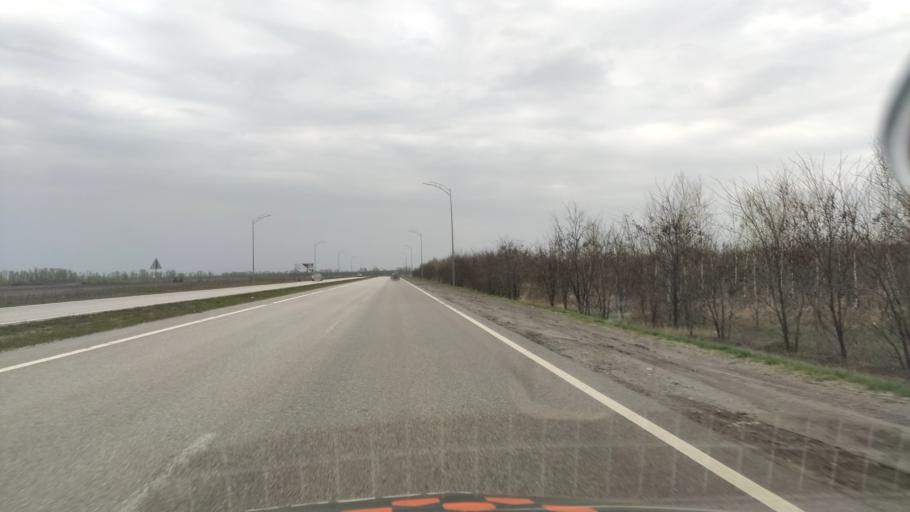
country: RU
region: Belgorod
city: Staryy Oskol
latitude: 51.3759
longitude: 37.8502
